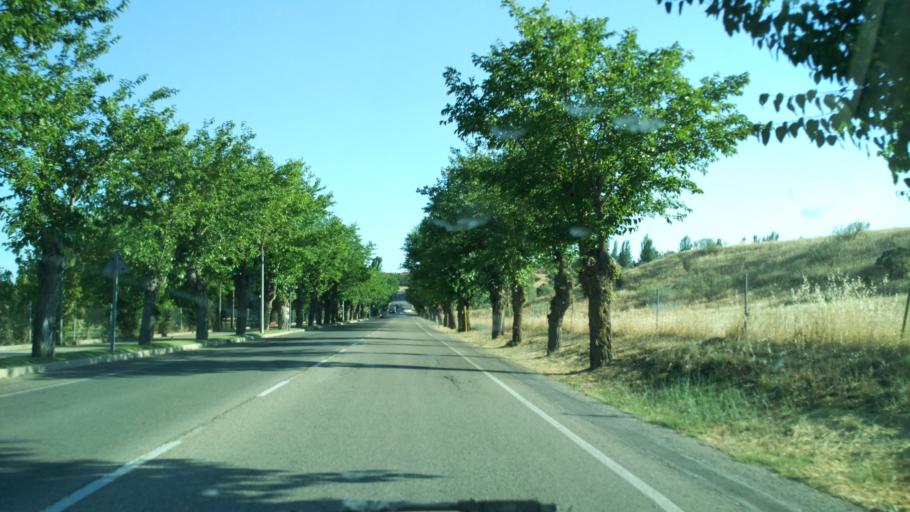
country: ES
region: Madrid
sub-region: Provincia de Madrid
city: San Agustin de Guadalix
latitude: 40.6884
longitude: -3.6104
